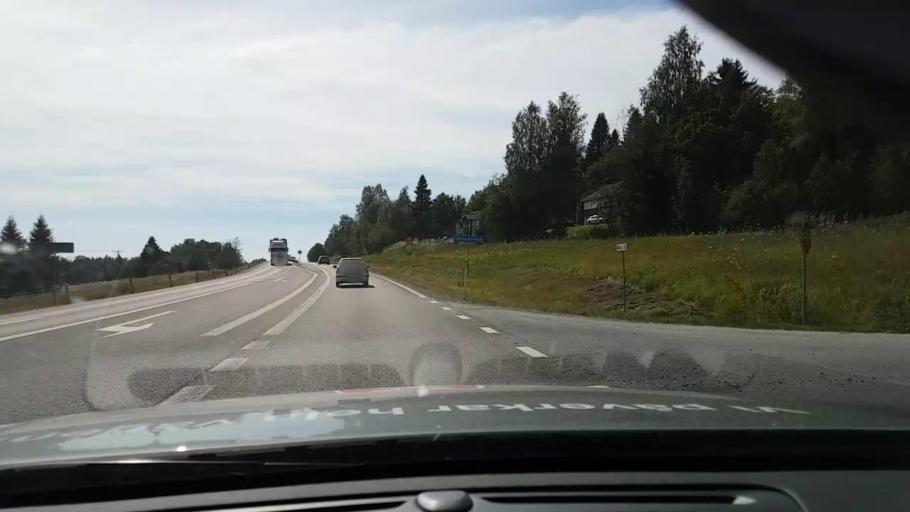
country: SE
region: Vaesternorrland
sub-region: OErnskoeldsviks Kommun
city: Ornskoldsvik
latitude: 63.3050
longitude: 18.9114
